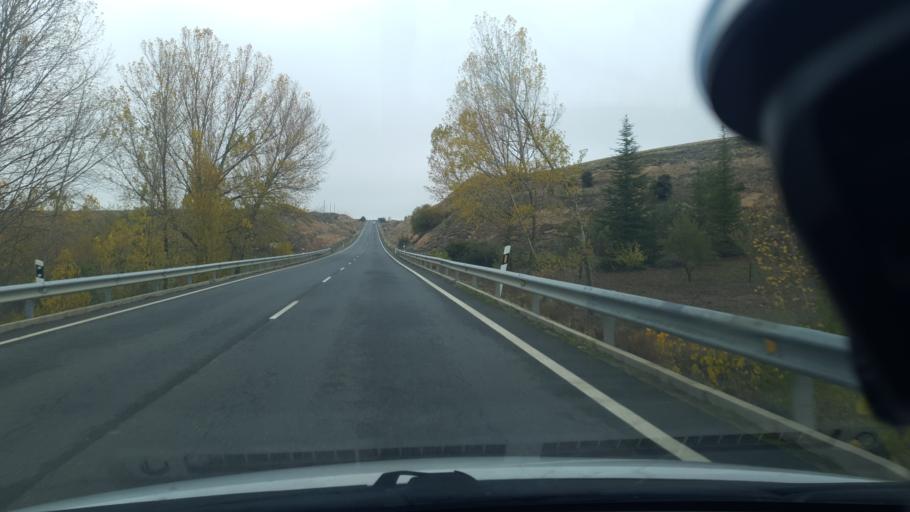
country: ES
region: Castille and Leon
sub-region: Provincia de Segovia
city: Encinillas
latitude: 41.0106
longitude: -4.1465
